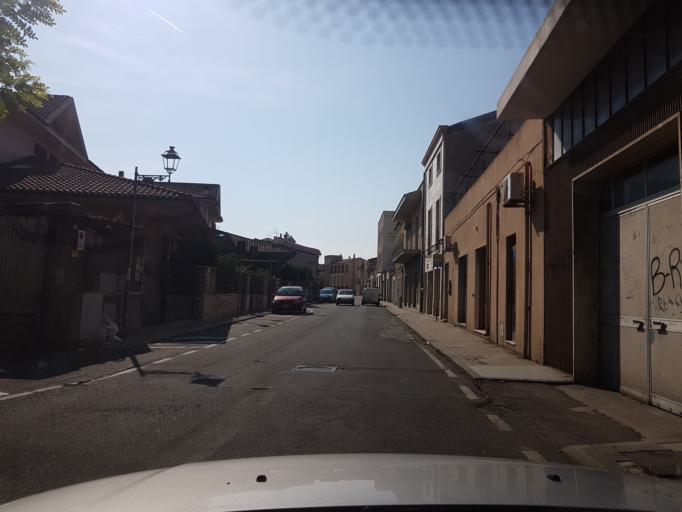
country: IT
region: Sardinia
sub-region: Provincia di Oristano
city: Oristano
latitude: 39.9006
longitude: 8.5921
